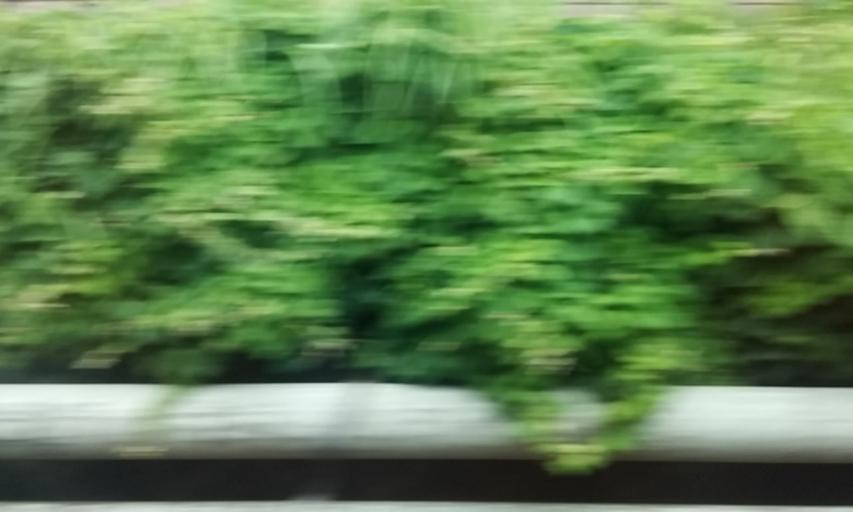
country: JP
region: Tokyo
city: Tokyo
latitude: 35.7060
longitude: 139.6776
